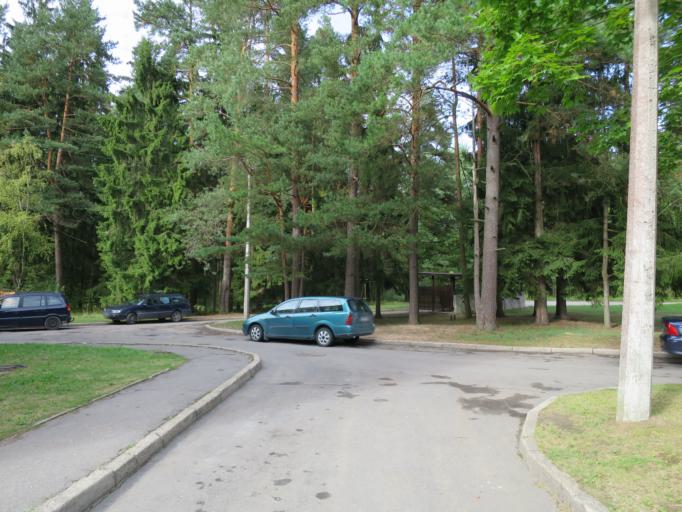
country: LV
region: Incukalns
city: Vangazi
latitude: 57.0962
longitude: 24.5431
